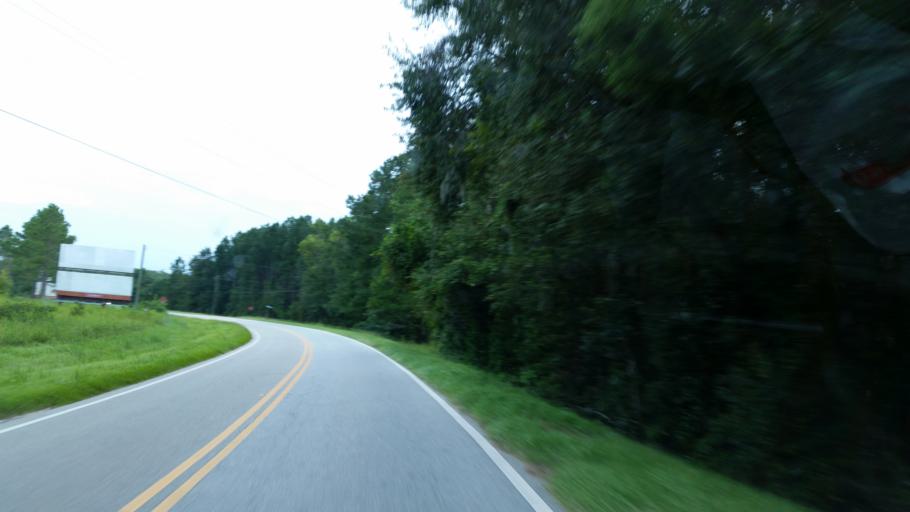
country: US
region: Georgia
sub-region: Lowndes County
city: Valdosta
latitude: 30.7730
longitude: -83.3027
